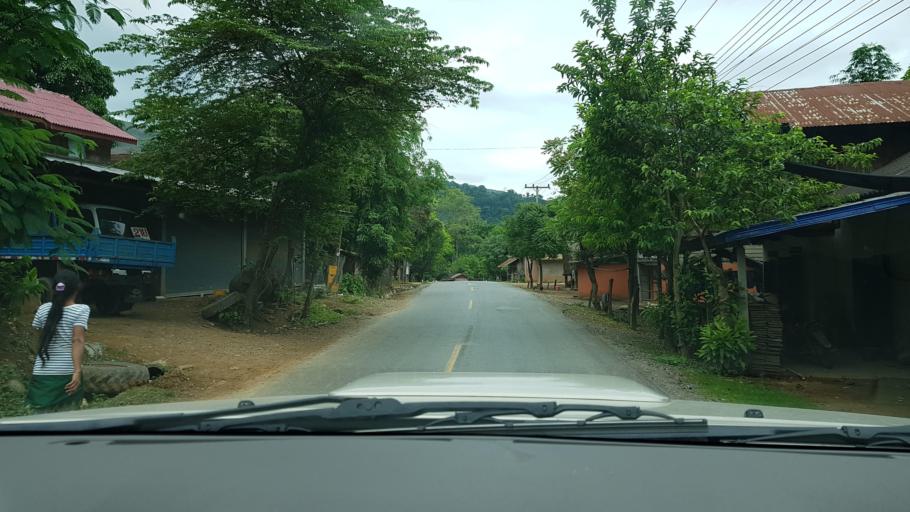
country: LA
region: Loungnamtha
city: Muang Nale
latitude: 20.1878
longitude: 101.5185
